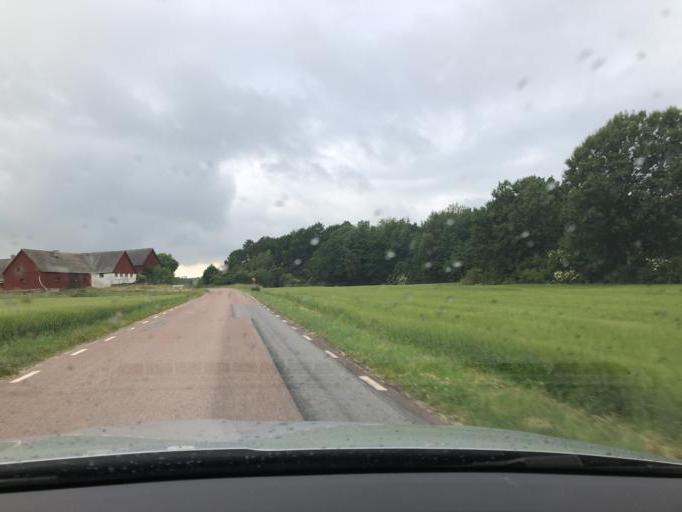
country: SE
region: Blekinge
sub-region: Solvesborgs Kommun
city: Soelvesborg
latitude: 56.1181
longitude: 14.6215
